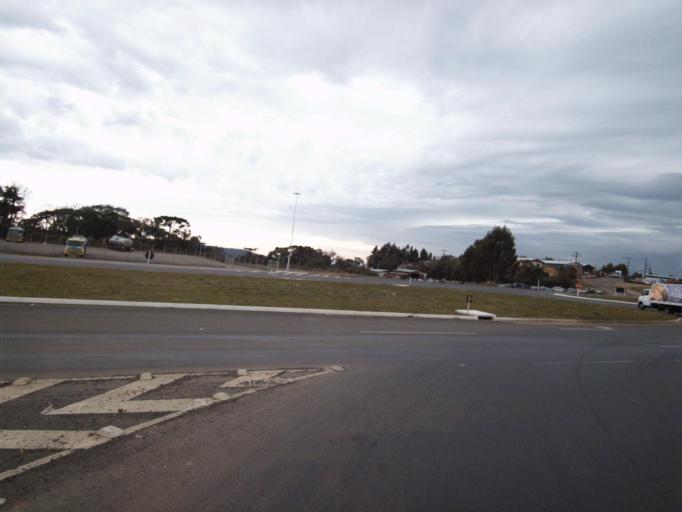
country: BR
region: Santa Catarina
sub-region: Concordia
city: Concordia
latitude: -27.0244
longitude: -51.8860
